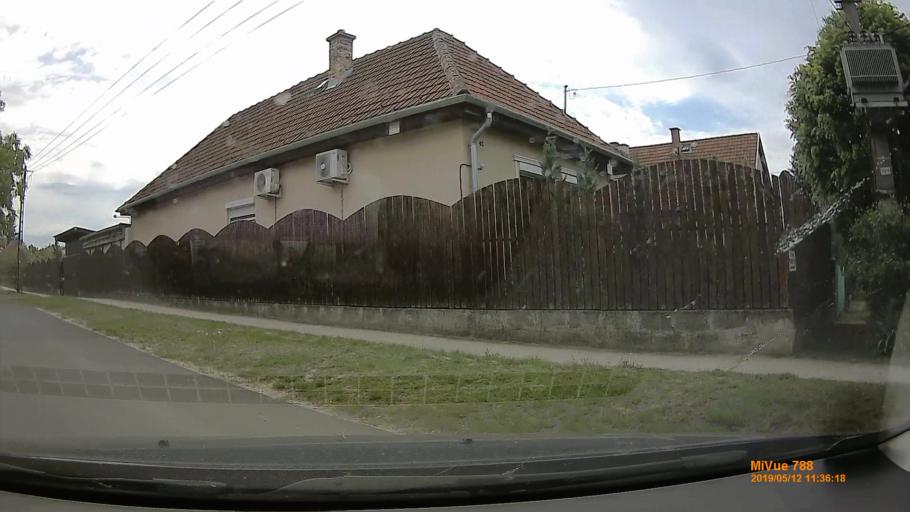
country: HU
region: Budapest
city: Budapest XVII. keruelet
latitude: 47.4650
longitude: 19.2532
